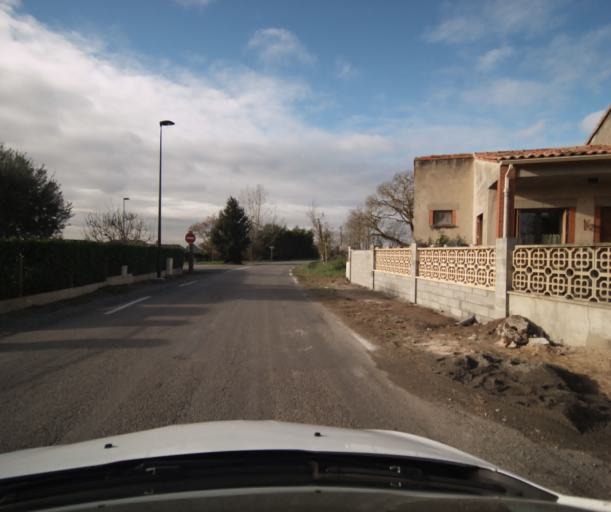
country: FR
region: Midi-Pyrenees
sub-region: Departement de la Haute-Garonne
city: Bruguieres
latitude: 43.7331
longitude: 1.4030
